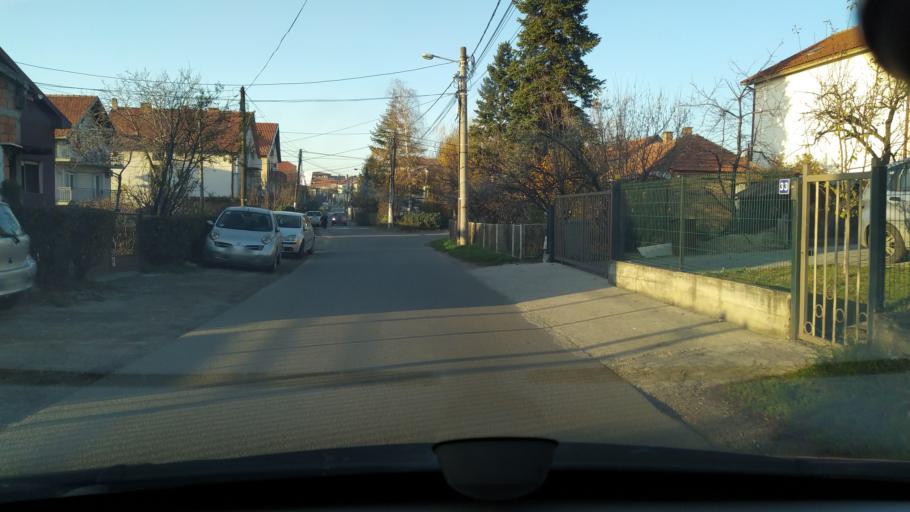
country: RS
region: Central Serbia
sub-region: Belgrade
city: Zvezdara
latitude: 44.7614
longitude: 20.5639
